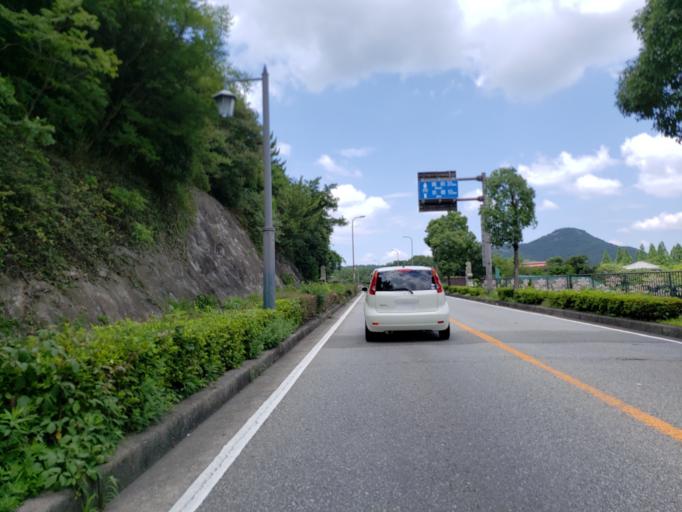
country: JP
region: Hyogo
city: Aioi
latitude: 34.8032
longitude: 134.4657
